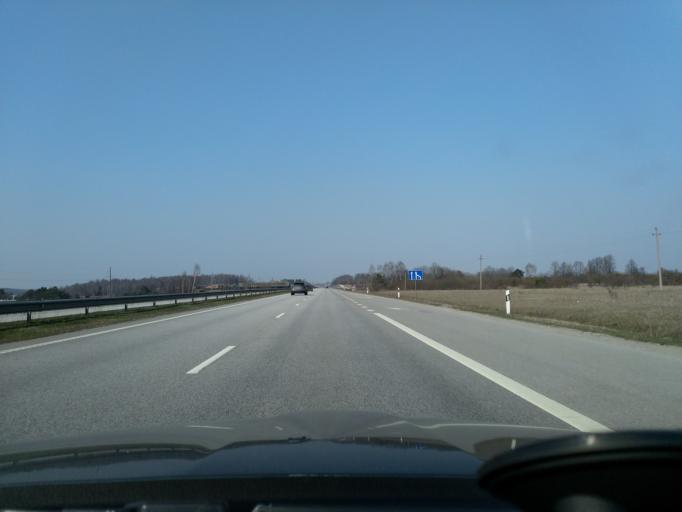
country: LT
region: Klaipedos apskritis
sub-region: Klaipeda
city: Klaipeda
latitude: 55.7614
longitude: 21.1656
